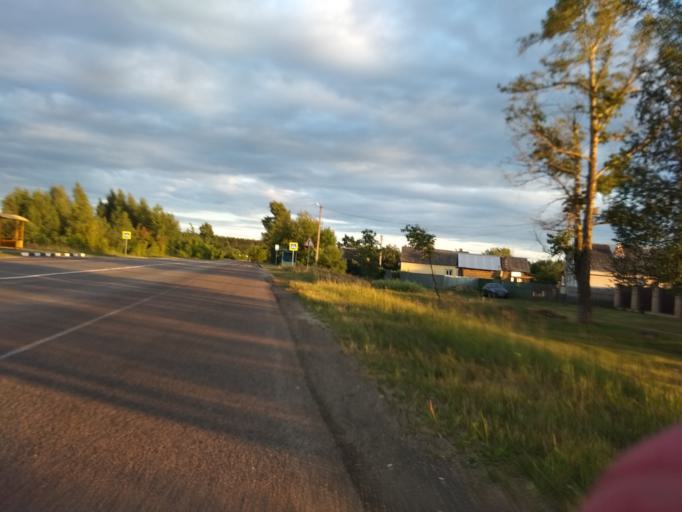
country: RU
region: Moskovskaya
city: Kerva
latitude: 55.5908
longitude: 39.7008
